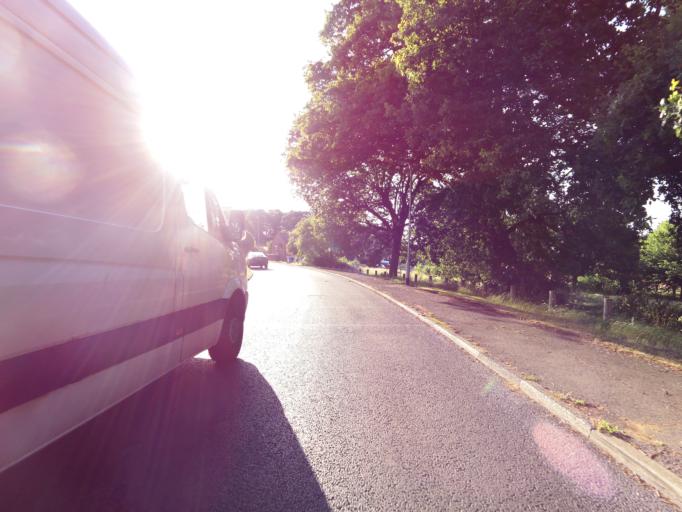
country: GB
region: England
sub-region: Suffolk
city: Ipswich
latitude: 52.0508
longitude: 1.1336
